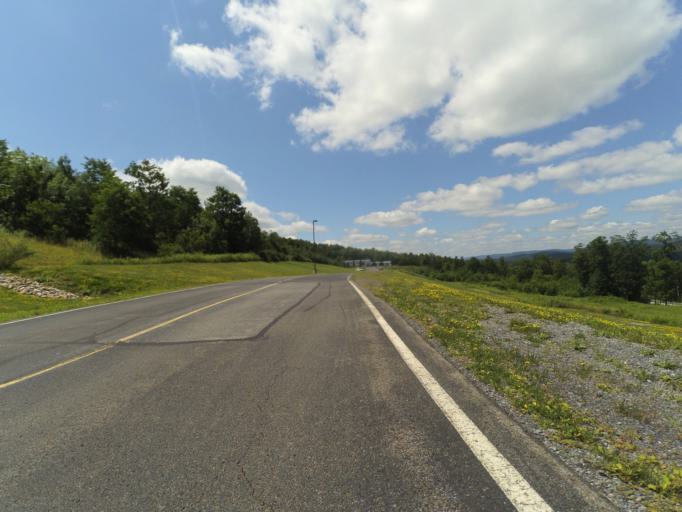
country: US
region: Pennsylvania
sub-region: Centre County
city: Stormstown
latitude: 40.8285
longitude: -77.9973
